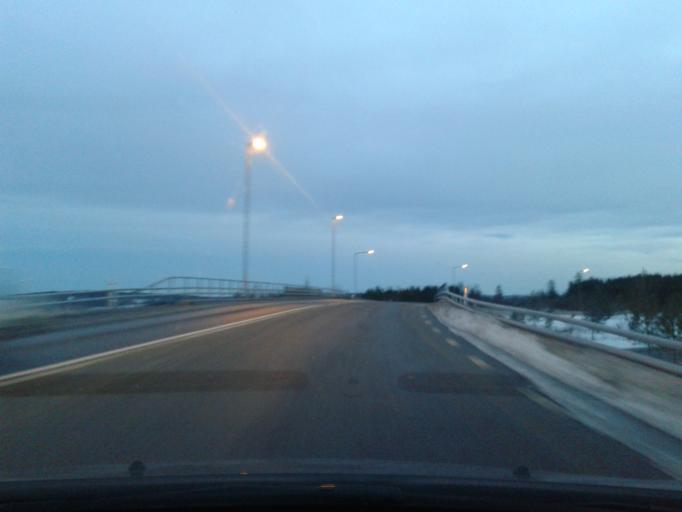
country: SE
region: Vaesternorrland
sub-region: Haernoesands Kommun
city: Haernoesand
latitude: 62.7857
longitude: 17.9187
